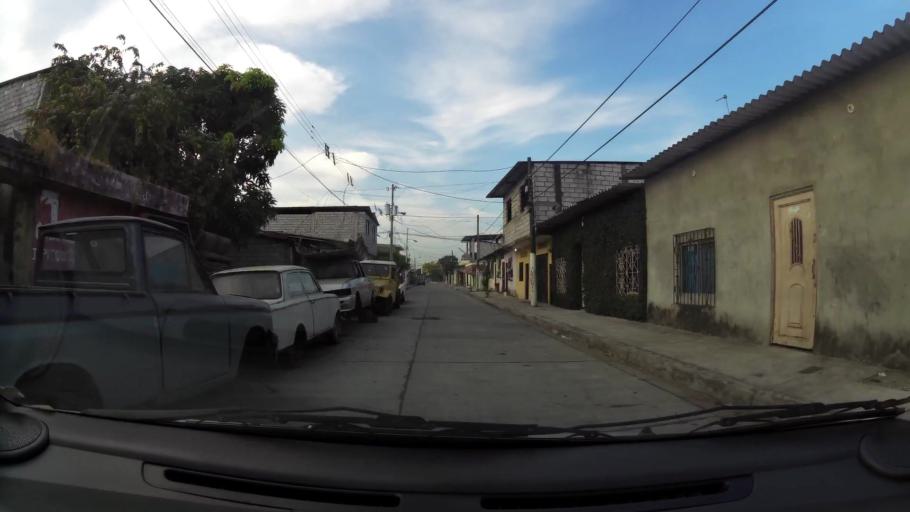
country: EC
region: Guayas
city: Eloy Alfaro
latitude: -2.0906
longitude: -79.9081
